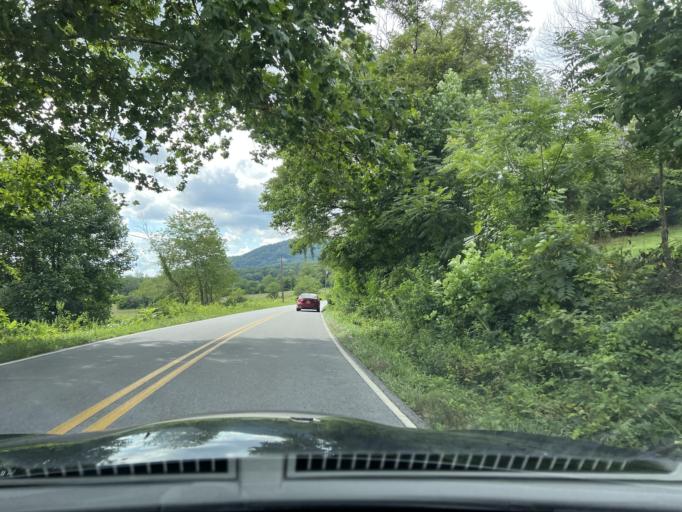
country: US
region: North Carolina
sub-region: Henderson County
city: Hoopers Creek
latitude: 35.4359
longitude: -82.4321
